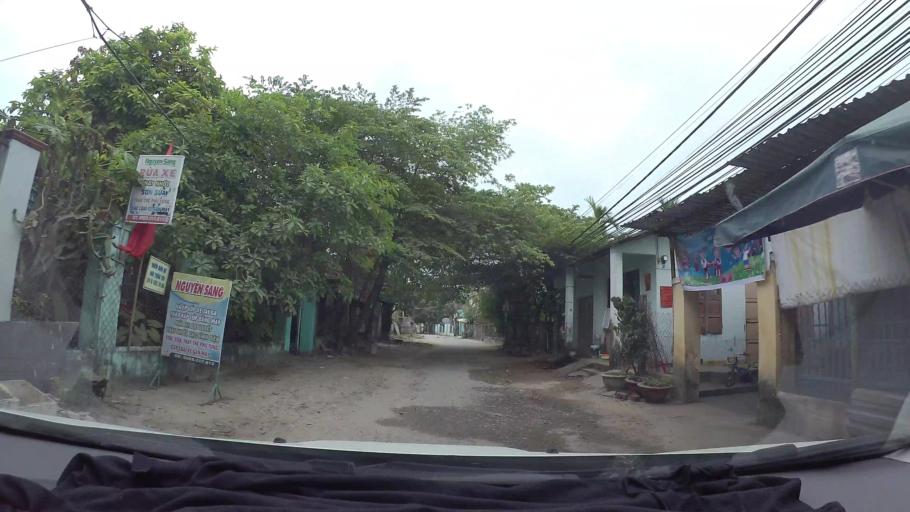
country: VN
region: Da Nang
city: Lien Chieu
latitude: 16.0597
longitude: 108.1673
